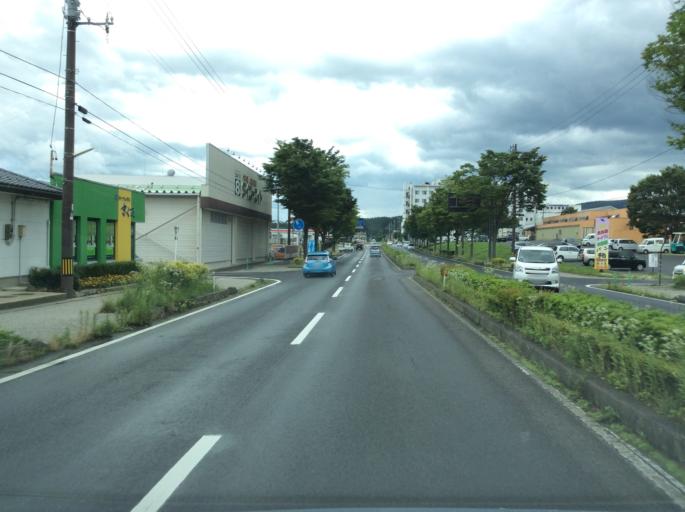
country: JP
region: Fukushima
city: Fukushima-shi
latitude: 37.7290
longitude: 140.3874
